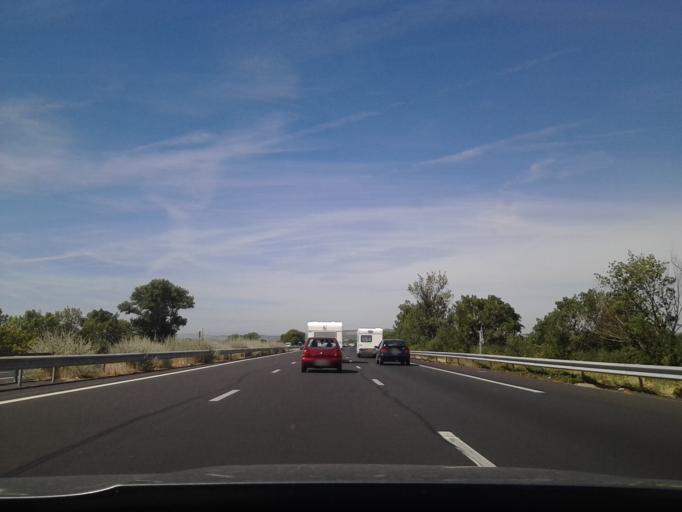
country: FR
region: Languedoc-Roussillon
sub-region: Departement de l'Aude
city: Vinassan
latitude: 43.1874
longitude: 3.0612
